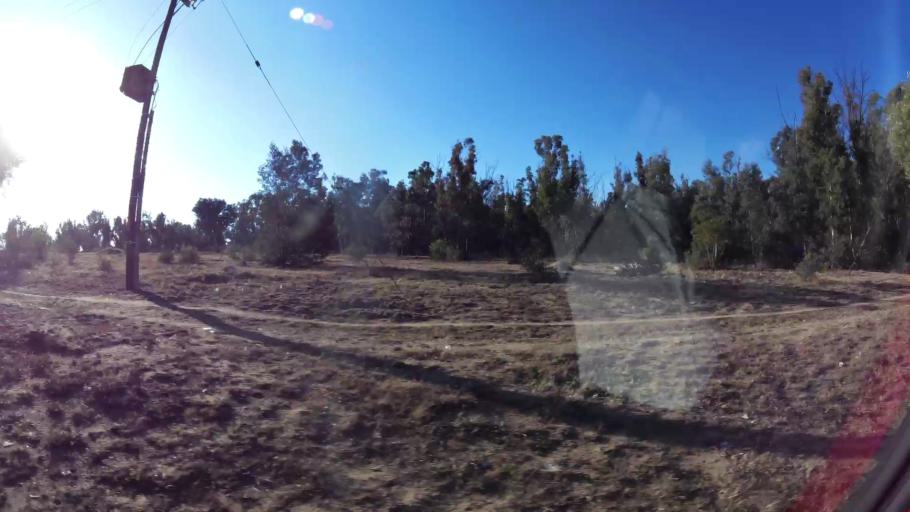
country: ZA
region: Gauteng
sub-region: City of Johannesburg Metropolitan Municipality
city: Midrand
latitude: -25.9810
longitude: 28.0905
